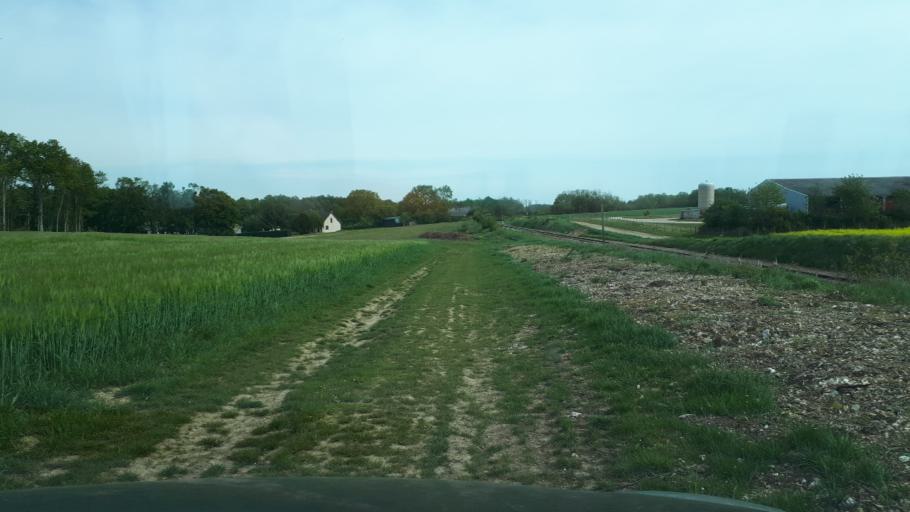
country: FR
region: Centre
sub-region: Departement du Loir-et-Cher
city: Naveil
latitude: 47.7688
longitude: 1.0172
